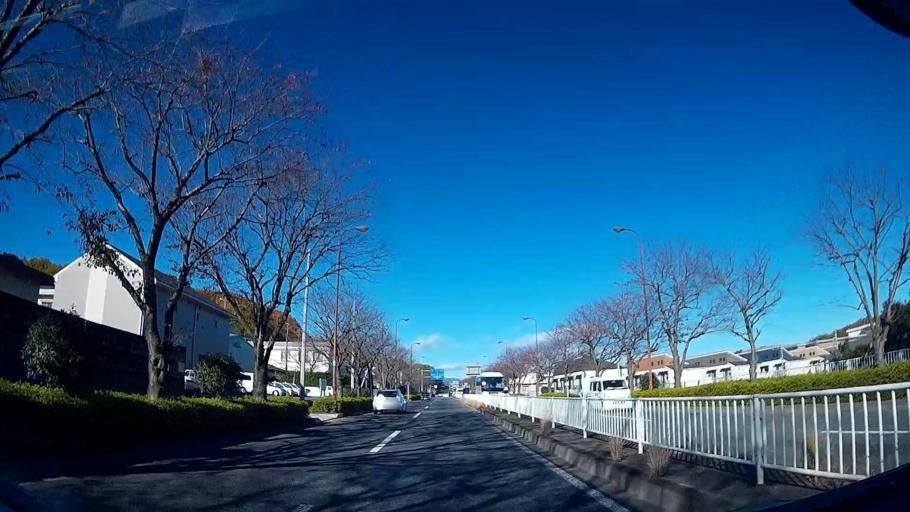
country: JP
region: Tokyo
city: Hachioji
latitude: 35.6888
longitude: 139.3354
